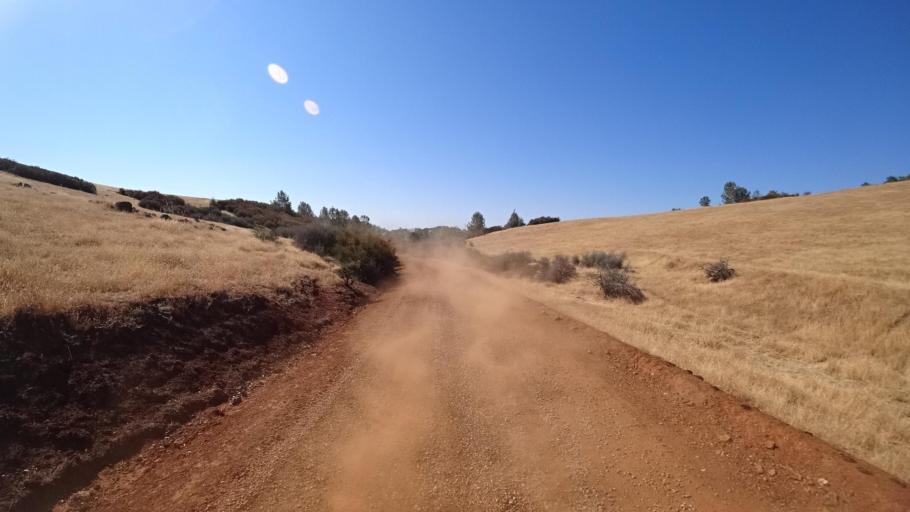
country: US
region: California
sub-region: Mariposa County
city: Mariposa
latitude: 37.6299
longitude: -120.2463
